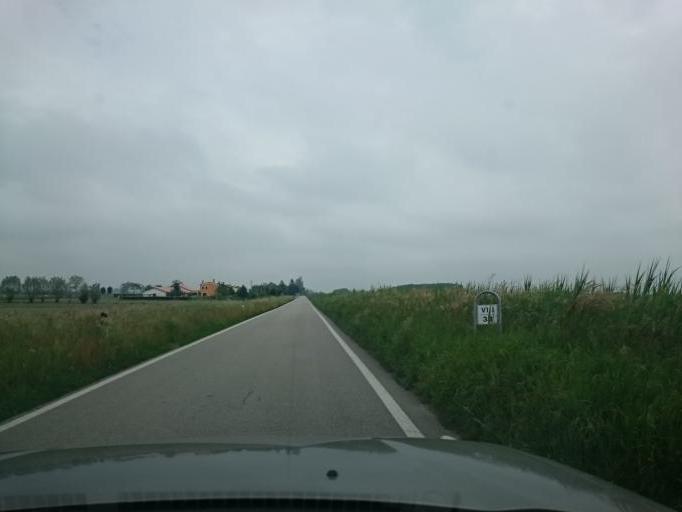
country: IT
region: Veneto
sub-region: Provincia di Venezia
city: Valli
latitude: 45.2113
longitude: 12.1369
